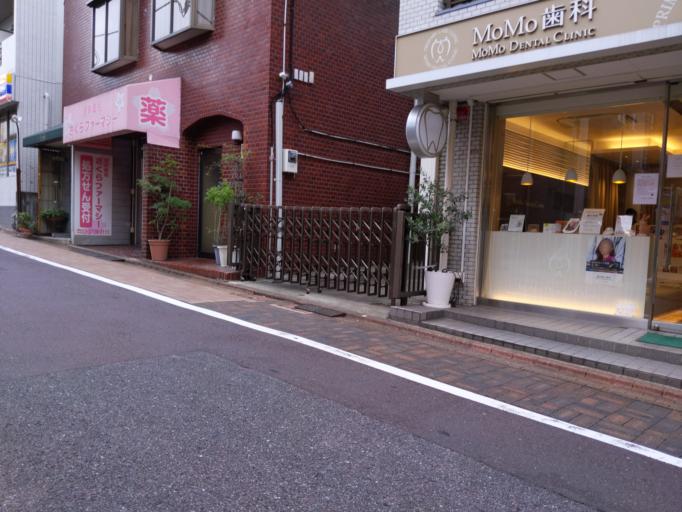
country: JP
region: Kanagawa
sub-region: Kawasaki-shi
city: Kawasaki
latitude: 35.5988
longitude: 139.6924
